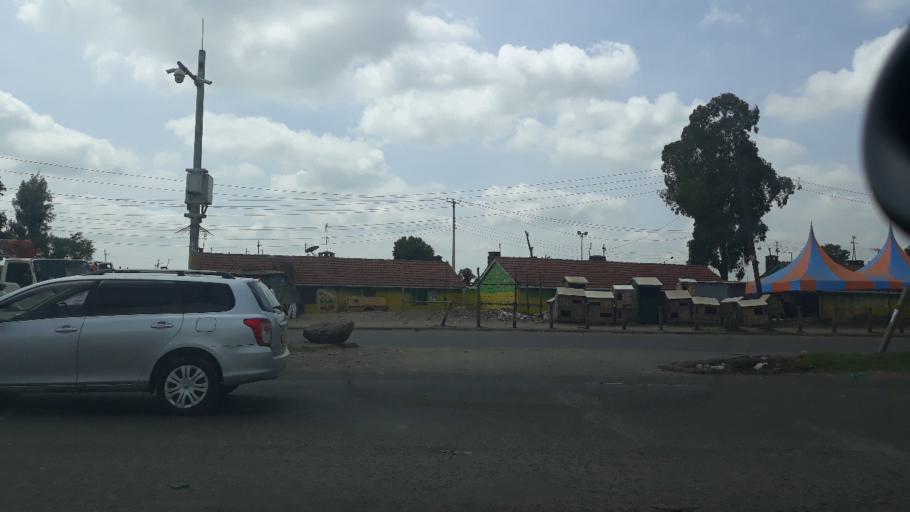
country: KE
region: Nairobi Area
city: Pumwani
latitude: -1.2974
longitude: 36.8673
